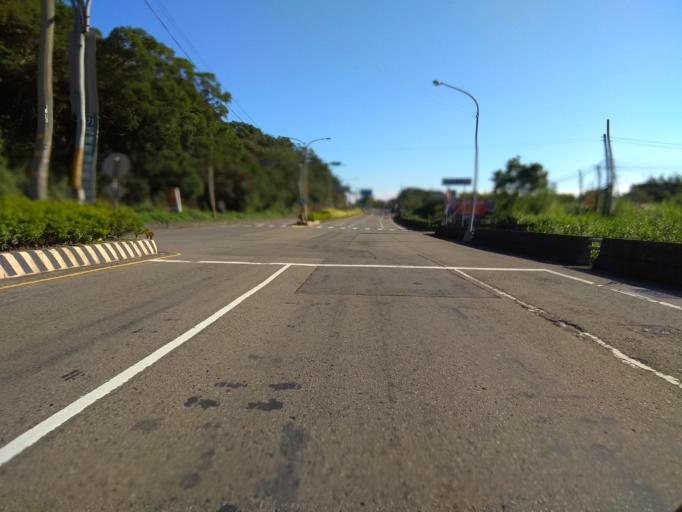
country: TW
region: Taiwan
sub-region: Hsinchu
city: Zhubei
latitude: 24.8948
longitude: 121.1078
